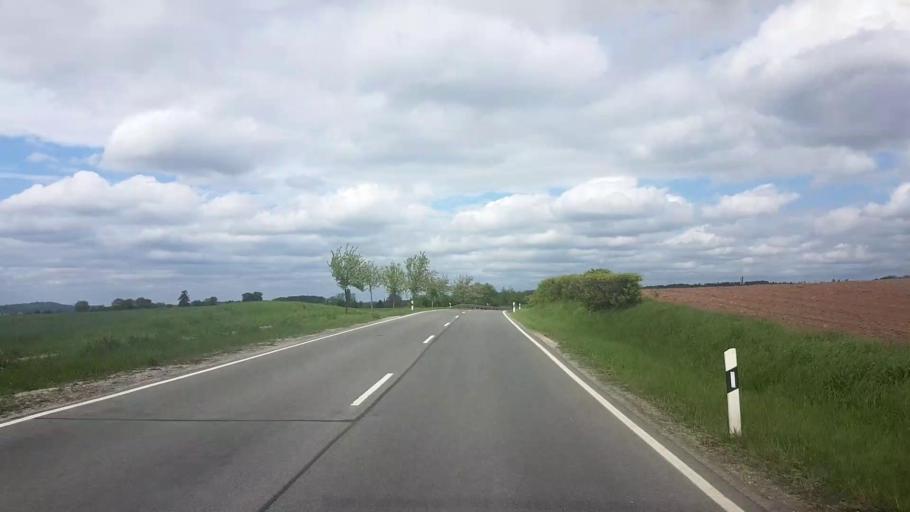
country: DE
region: Bavaria
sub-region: Upper Franconia
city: Untersiemau
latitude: 50.1794
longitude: 11.0185
